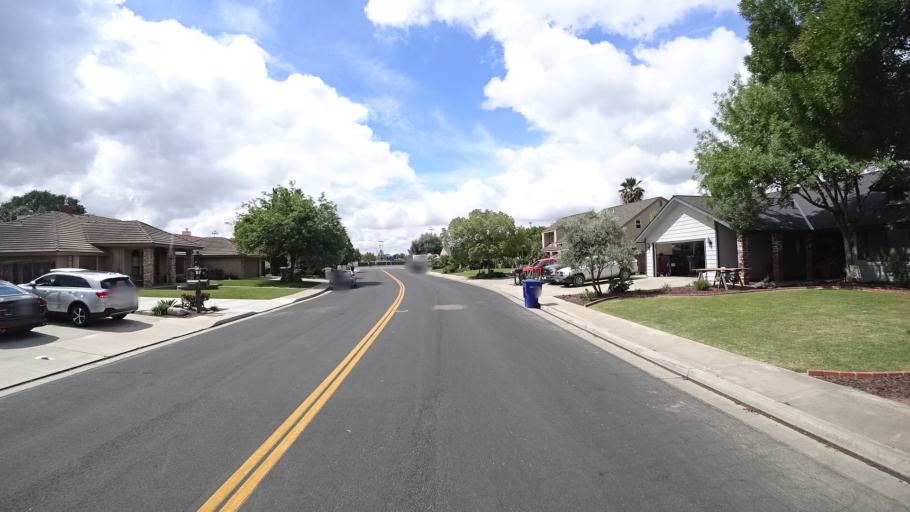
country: US
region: California
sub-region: Kings County
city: Hanford
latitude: 36.3370
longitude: -119.6647
